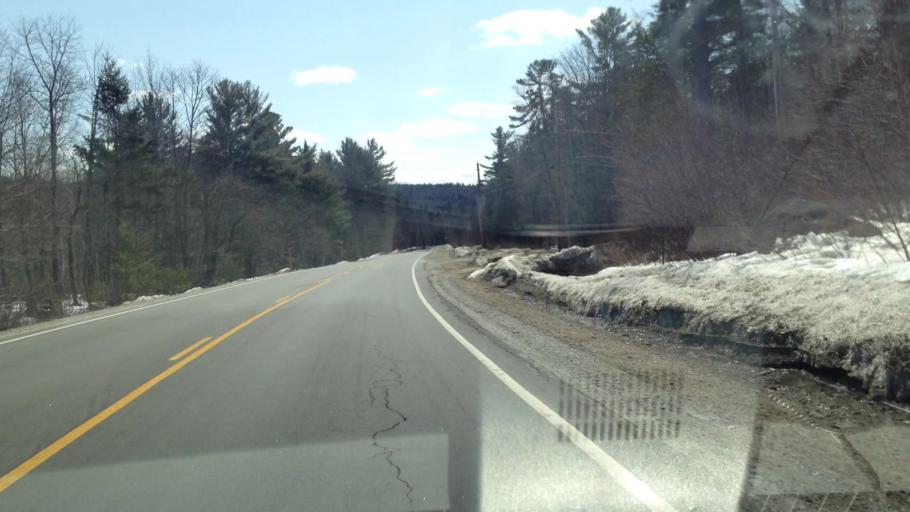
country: US
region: New Hampshire
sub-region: Merrimack County
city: Wilmot
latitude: 43.4734
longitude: -71.9637
